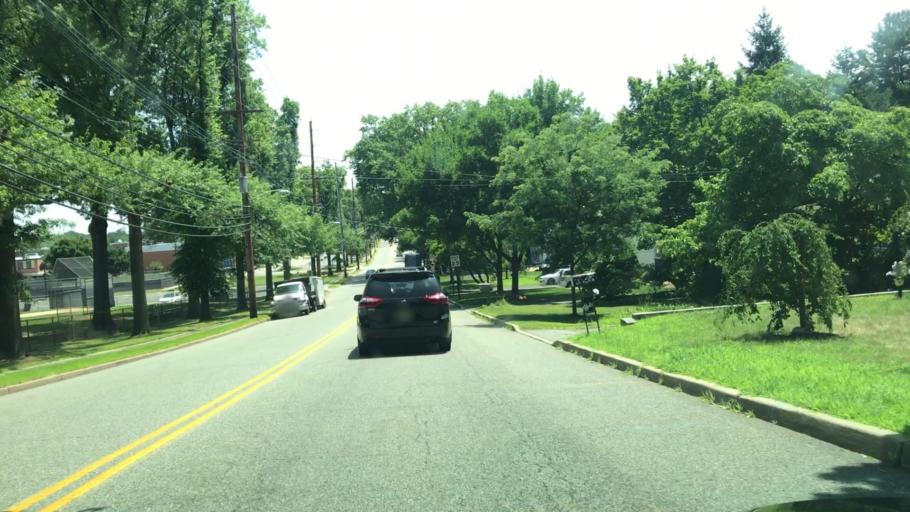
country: US
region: New Jersey
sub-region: Bergen County
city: Paramus
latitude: 40.9279
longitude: -74.0645
